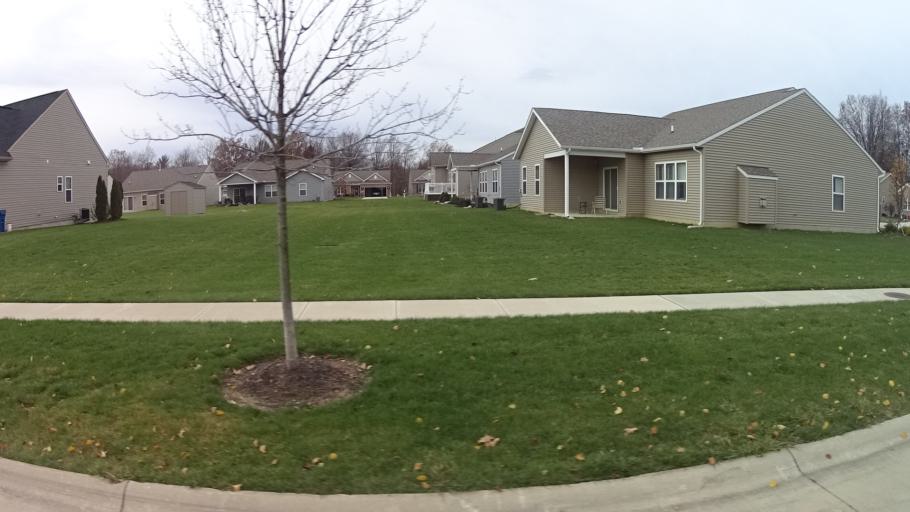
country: US
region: Ohio
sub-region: Lorain County
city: North Ridgeville
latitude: 41.3875
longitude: -82.0559
